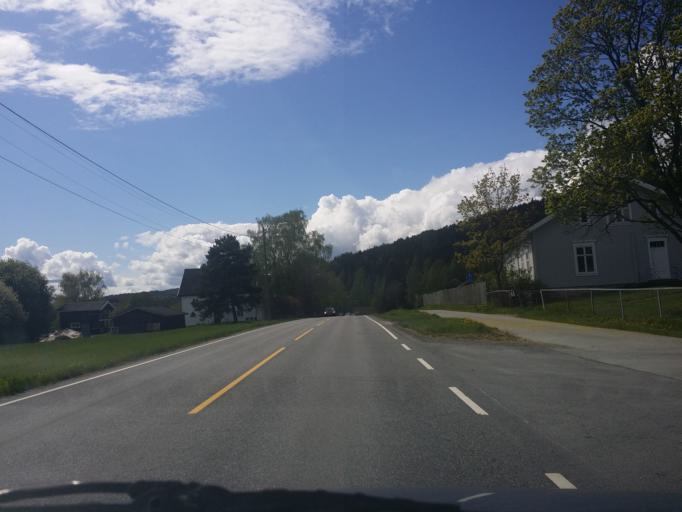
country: NO
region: Buskerud
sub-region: Ringerike
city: Honefoss
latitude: 60.1352
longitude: 10.1672
